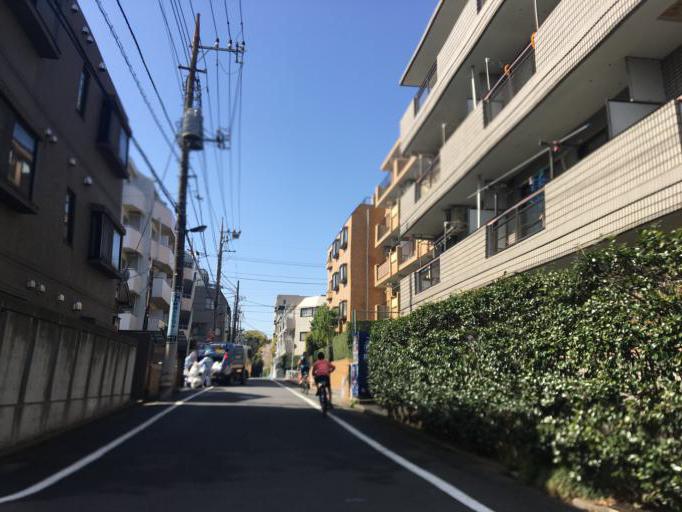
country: JP
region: Saitama
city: Wako
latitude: 35.7718
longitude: 139.6330
